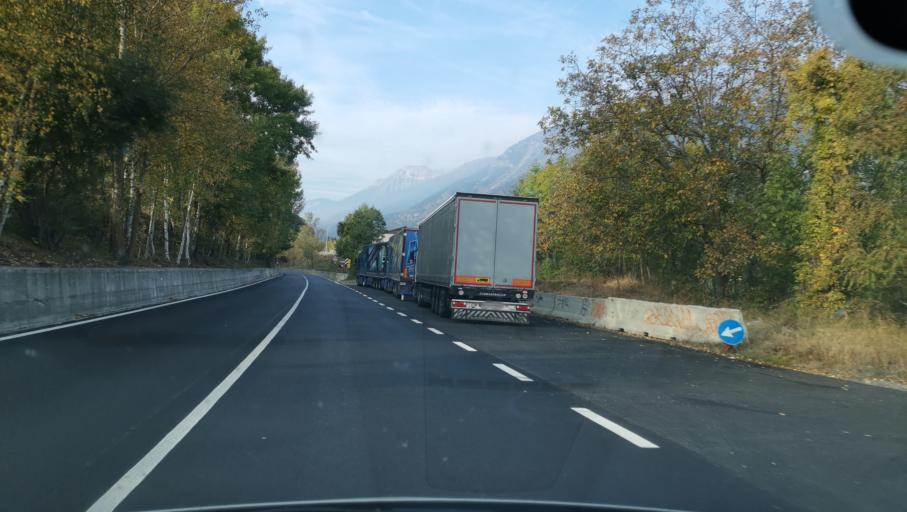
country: IT
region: Piedmont
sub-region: Provincia di Torino
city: Gravere
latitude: 45.1260
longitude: 7.0053
